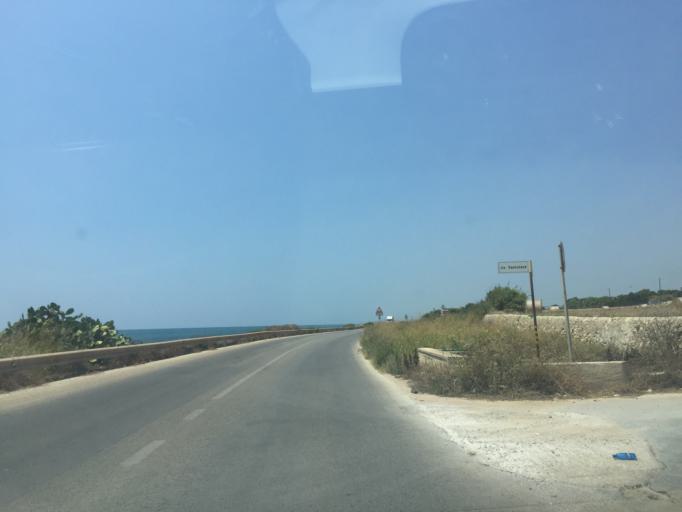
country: IT
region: Sicily
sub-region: Ragusa
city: Donnalucata
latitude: 36.7659
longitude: 14.6212
